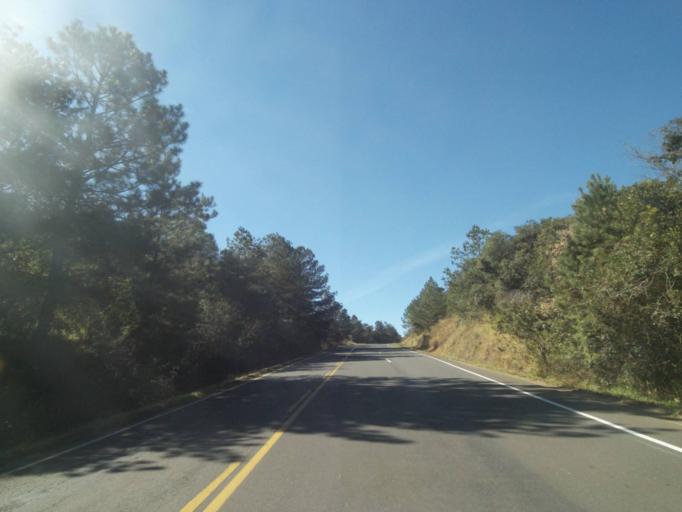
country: BR
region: Parana
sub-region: Tibagi
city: Tibagi
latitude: -24.4728
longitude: -50.5263
